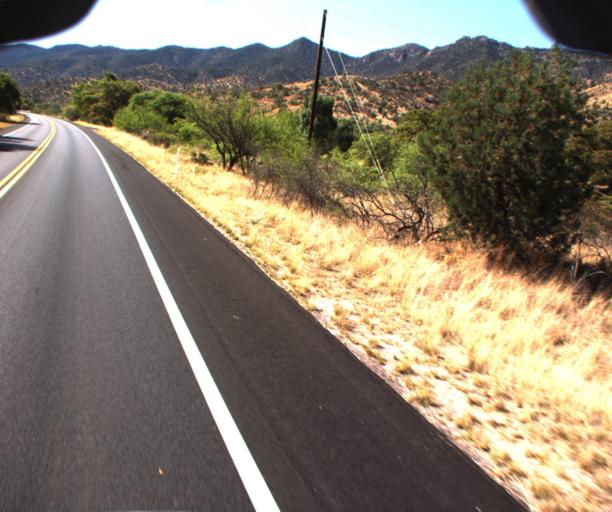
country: US
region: Arizona
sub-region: Cochise County
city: Bisbee
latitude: 31.4911
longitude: -109.9899
